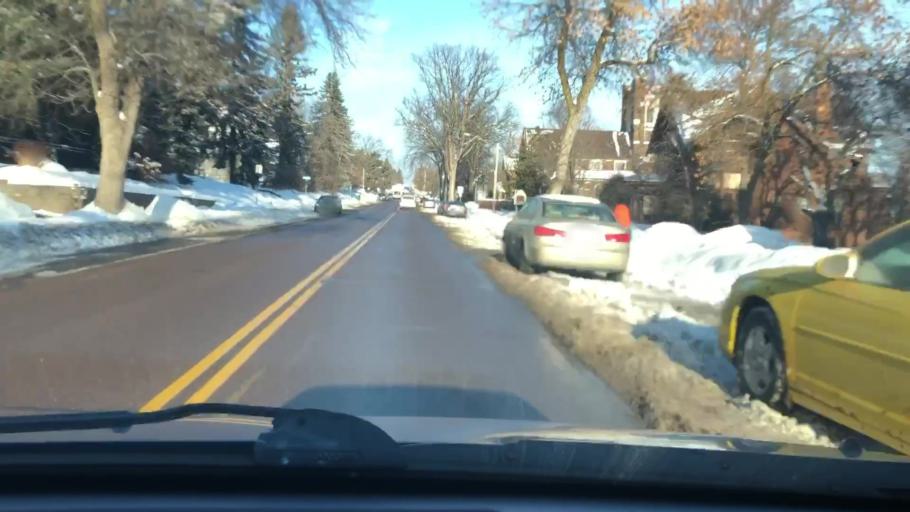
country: US
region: Minnesota
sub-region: Saint Louis County
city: Duluth
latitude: 46.8025
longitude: -92.0778
